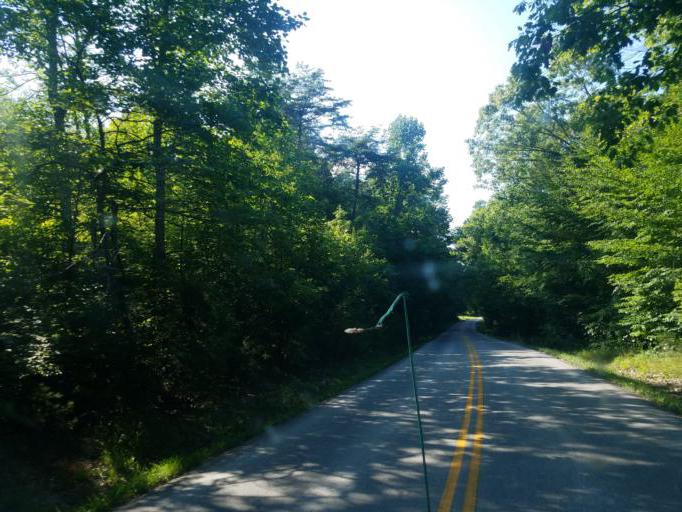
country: US
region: Kentucky
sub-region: Hart County
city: Munfordville
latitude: 37.3502
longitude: -86.0417
